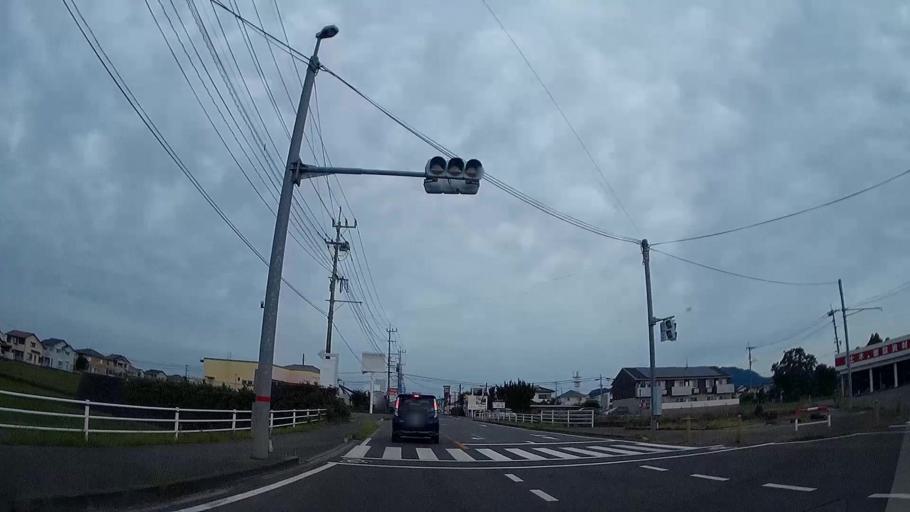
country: JP
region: Kumamoto
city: Kikuchi
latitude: 32.9725
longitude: 130.8094
